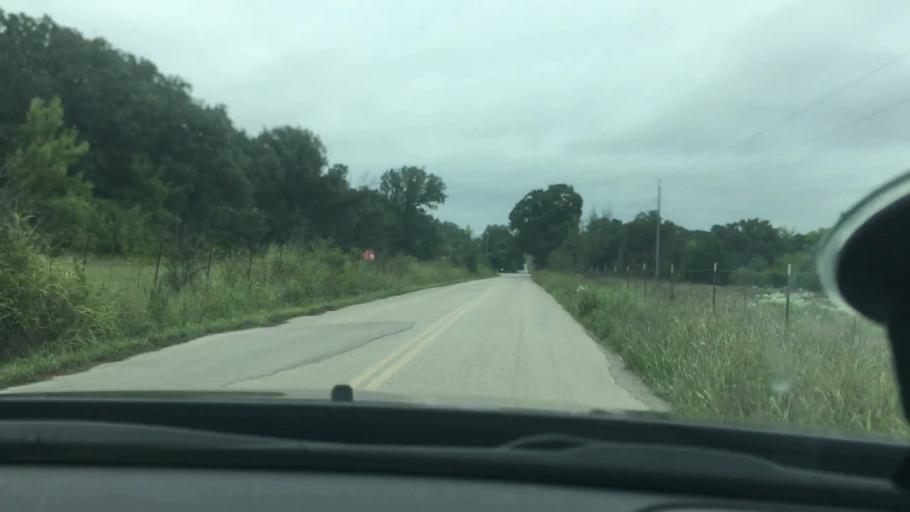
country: US
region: Oklahoma
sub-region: Pontotoc County
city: Ada
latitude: 34.8057
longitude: -96.7573
